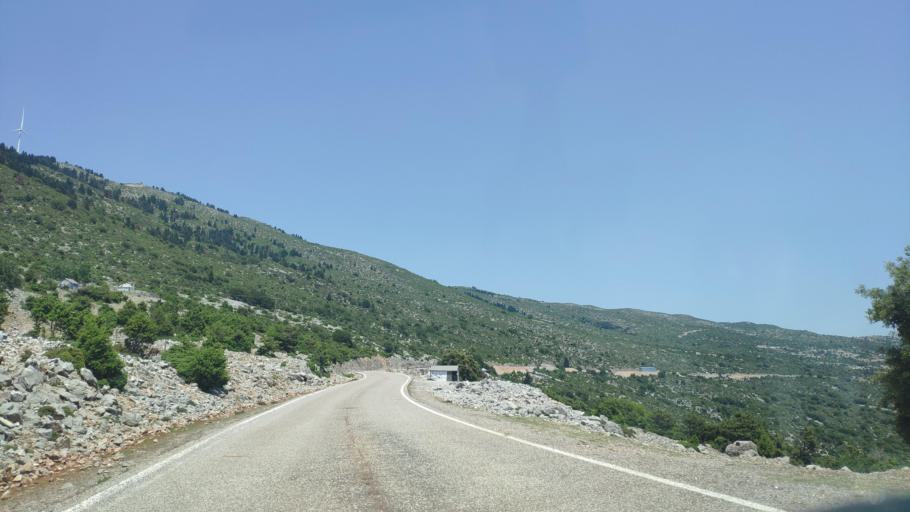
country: GR
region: West Greece
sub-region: Nomos Aitolias kai Akarnanias
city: Krikellos
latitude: 39.0599
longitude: 21.3837
